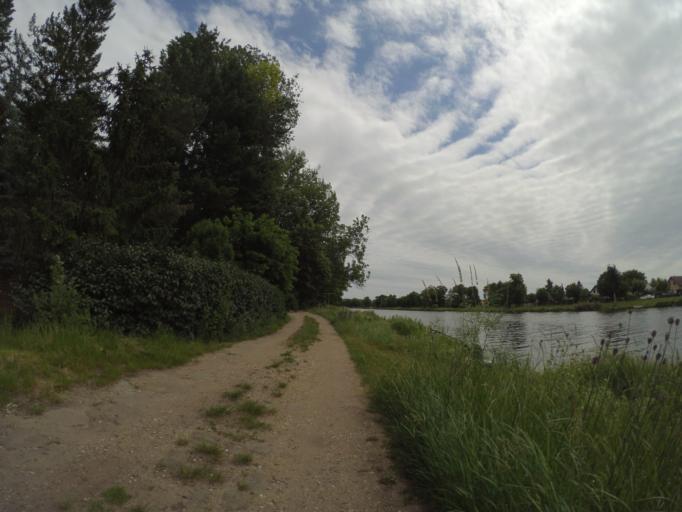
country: CZ
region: Central Bohemia
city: Celakovice
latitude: 50.1722
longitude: 14.7845
